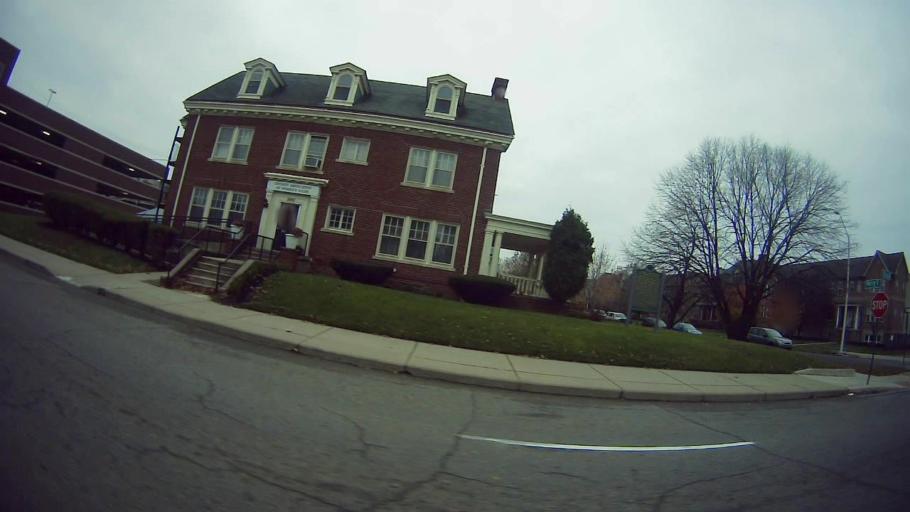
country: US
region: Michigan
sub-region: Wayne County
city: Hamtramck
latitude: 42.3627
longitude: -83.0625
